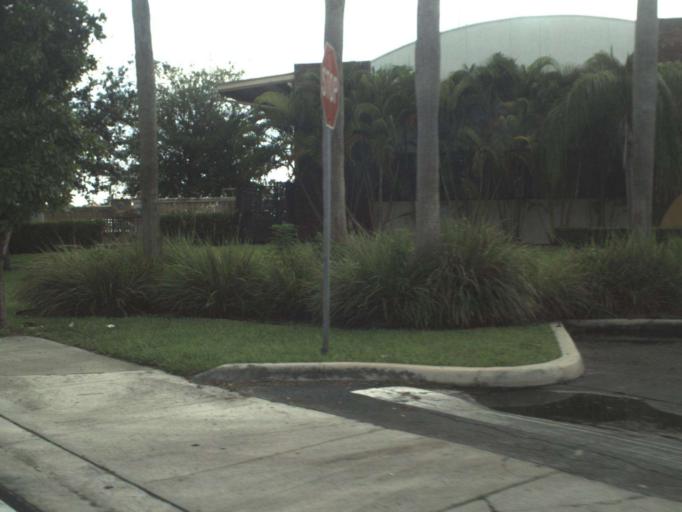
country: US
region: Florida
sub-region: Miami-Dade County
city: North Miami Beach
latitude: 25.9203
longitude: -80.1578
